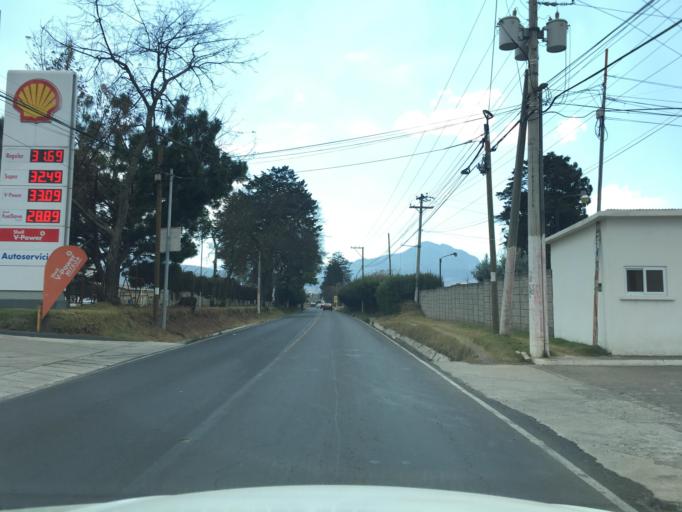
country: GT
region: Quetzaltenango
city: Olintepeque
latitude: 14.8720
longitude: -91.5133
